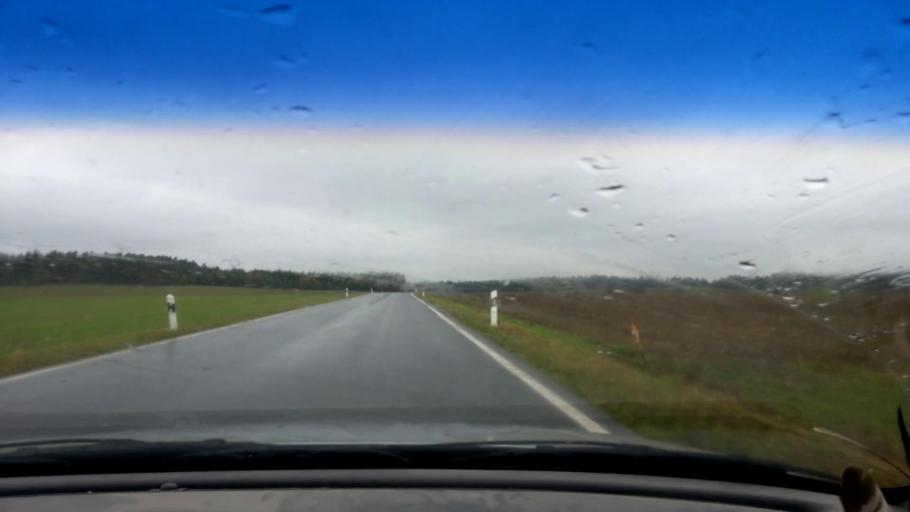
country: DE
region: Bavaria
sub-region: Upper Franconia
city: Poxdorf
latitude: 49.9113
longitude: 11.1456
